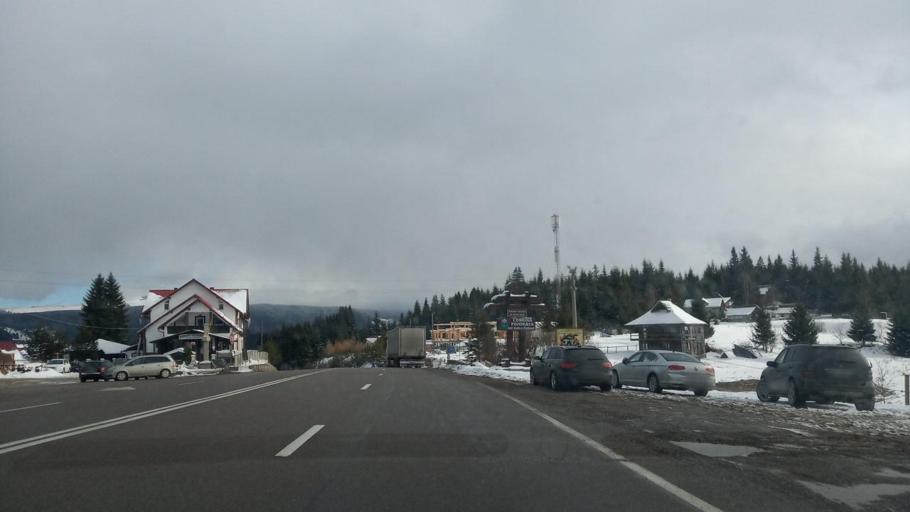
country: RO
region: Suceava
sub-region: Comuna Iacobeni
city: Iacobeni
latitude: 47.4641
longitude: 25.3465
